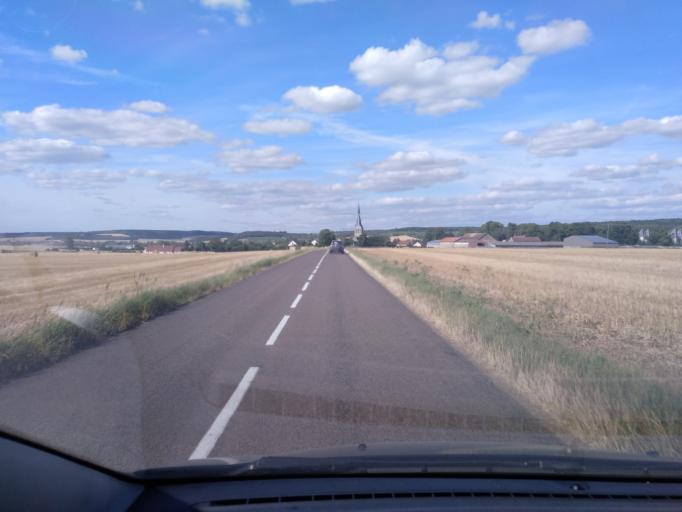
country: FR
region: Bourgogne
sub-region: Departement de la Cote-d'Or
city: Chatillon-sur-Seine
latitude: 47.9387
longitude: 4.6477
